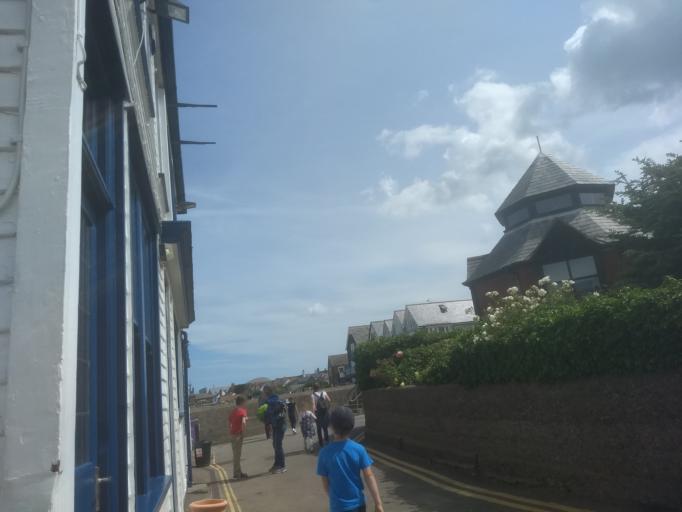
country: GB
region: England
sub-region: Kent
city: Whitstable
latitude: 51.3587
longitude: 1.0202
